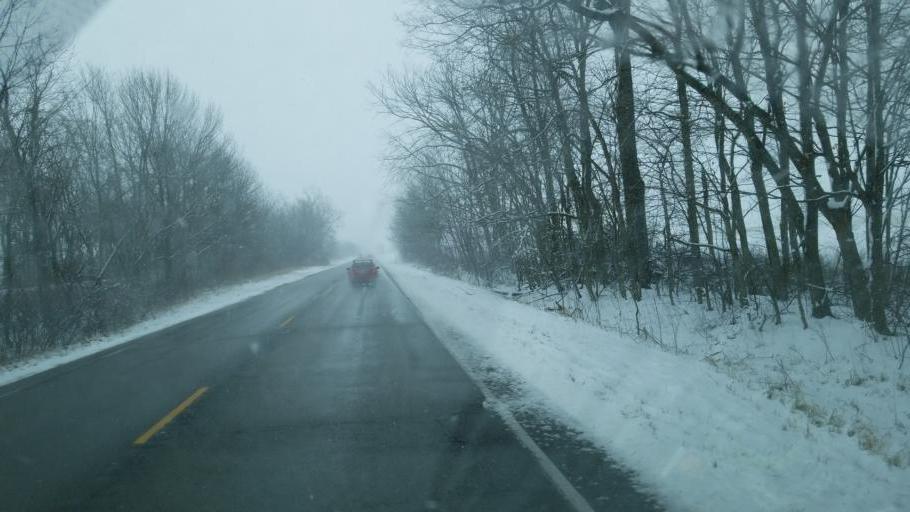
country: US
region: Indiana
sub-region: Wayne County
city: Hagerstown
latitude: 40.0400
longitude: -85.2098
